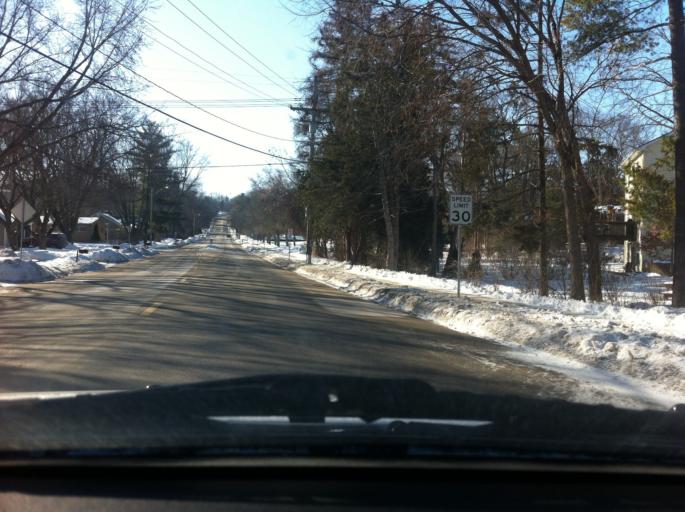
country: US
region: Wisconsin
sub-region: Dane County
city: Shorewood Hills
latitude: 43.0749
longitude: -89.4779
